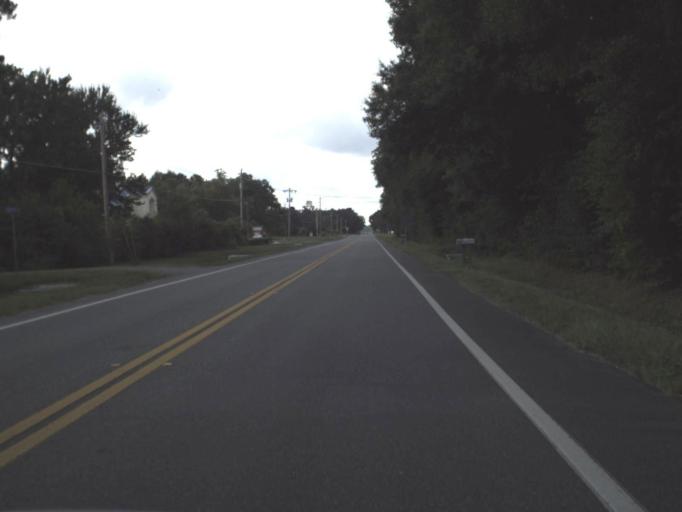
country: US
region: Florida
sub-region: Baker County
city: Macclenny
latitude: 30.3370
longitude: -82.1252
